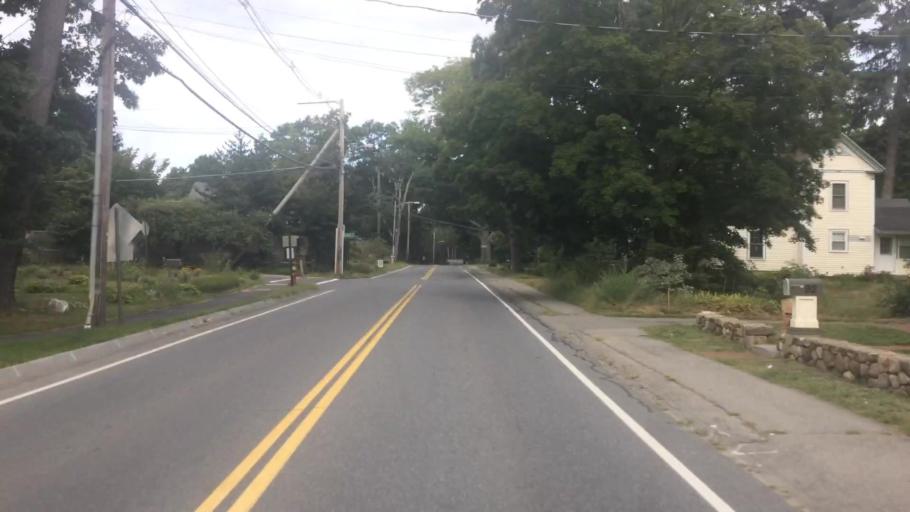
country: US
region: Massachusetts
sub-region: Middlesex County
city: West Concord
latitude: 42.4587
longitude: -71.4001
